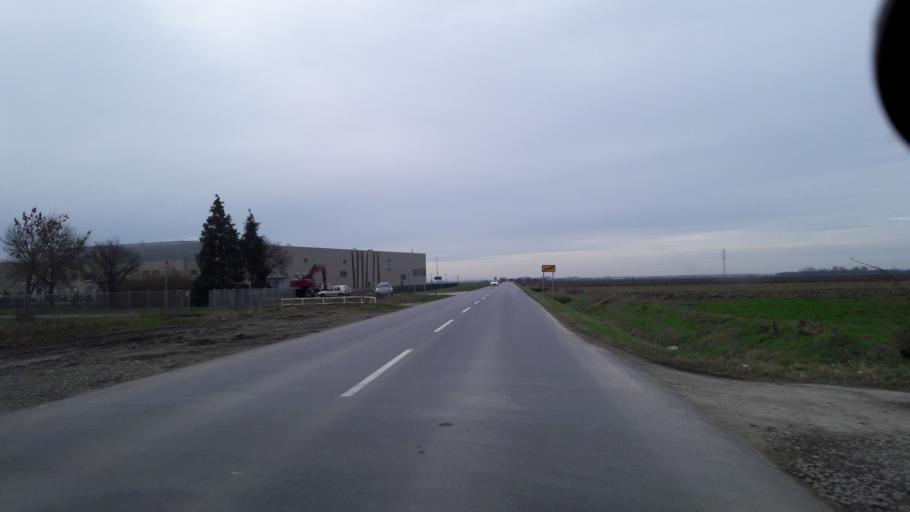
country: HR
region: Osjecko-Baranjska
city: Ovcara
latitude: 45.5032
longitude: 18.5608
